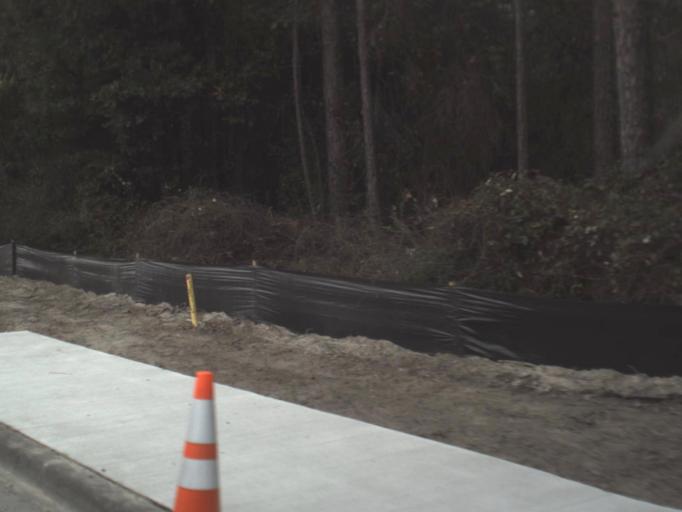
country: US
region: Florida
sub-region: Bay County
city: Springfield
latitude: 30.1650
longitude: -85.5912
